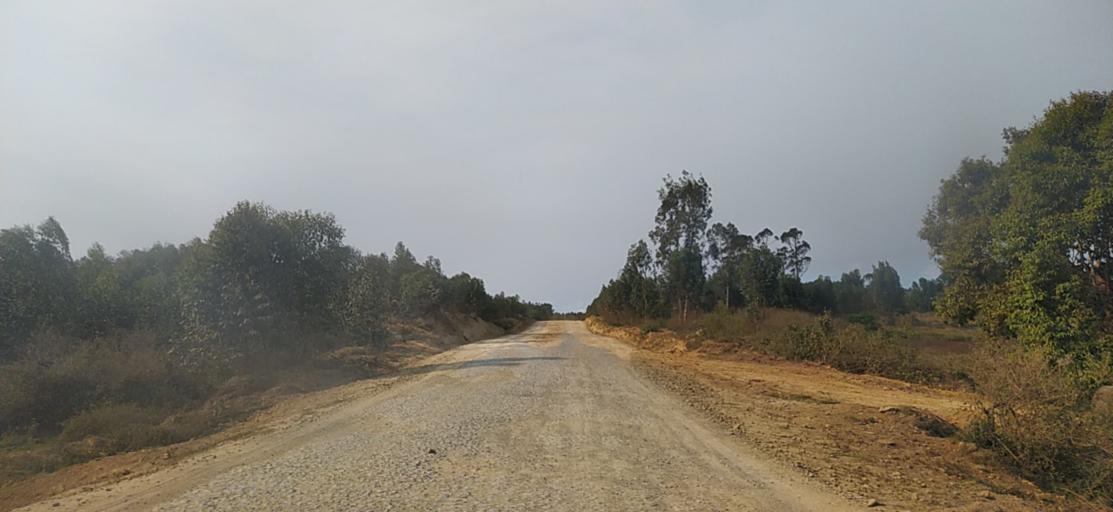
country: MG
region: Alaotra Mangoro
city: Moramanga
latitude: -18.6587
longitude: 48.2741
